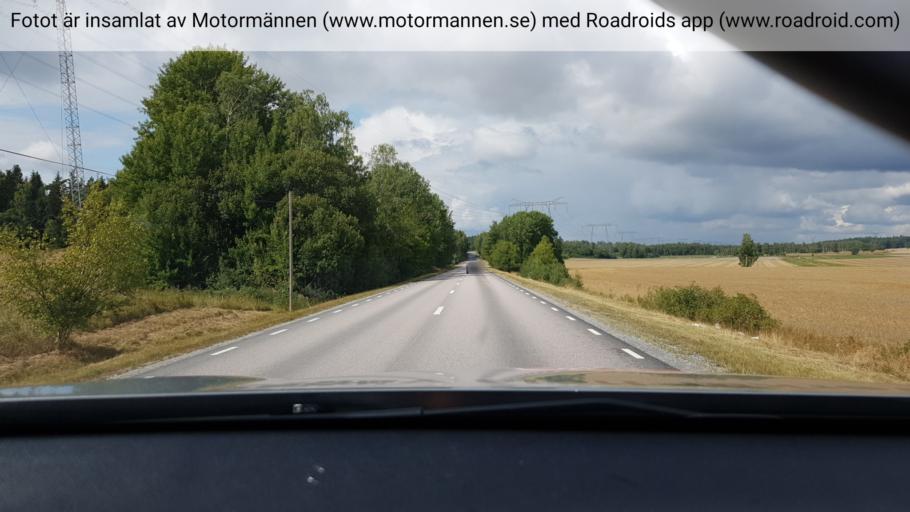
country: SE
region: Stockholm
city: Stenhamra
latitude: 59.3708
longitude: 17.6062
